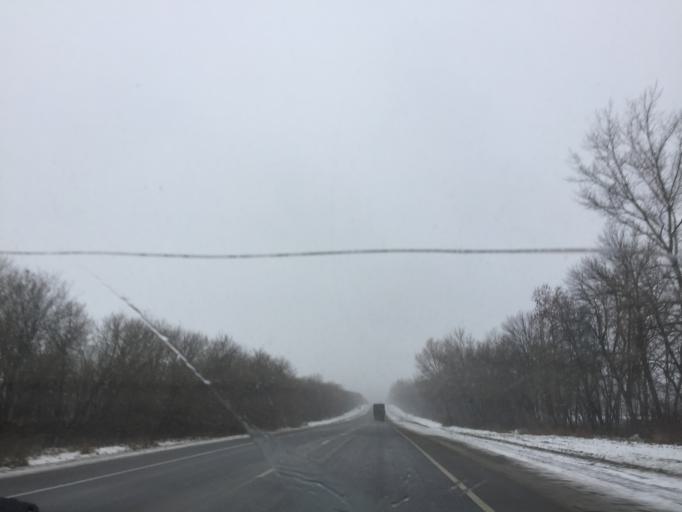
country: RU
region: Tula
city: Plavsk
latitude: 53.7665
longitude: 37.3440
